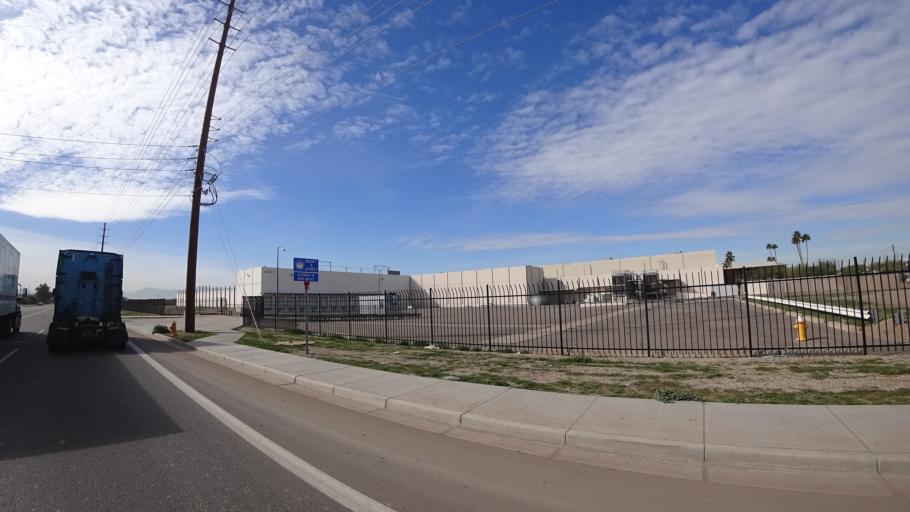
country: US
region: Arizona
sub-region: Maricopa County
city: Laveen
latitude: 33.4359
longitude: -112.1520
